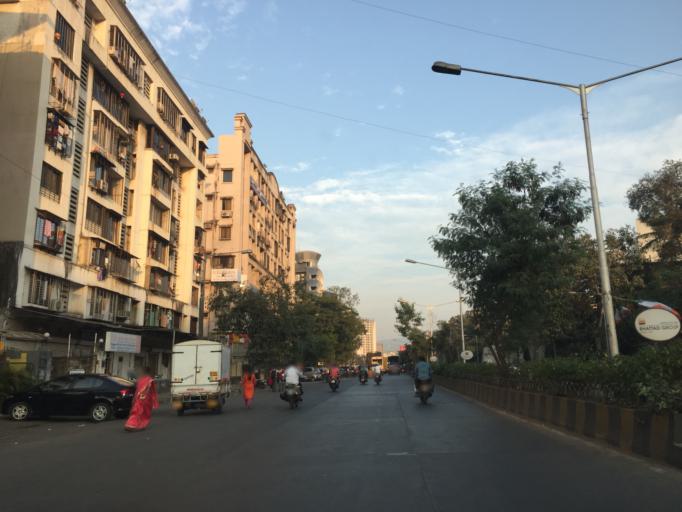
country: IN
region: Maharashtra
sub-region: Mumbai Suburban
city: Borivli
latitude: 19.2206
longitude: 72.8506
